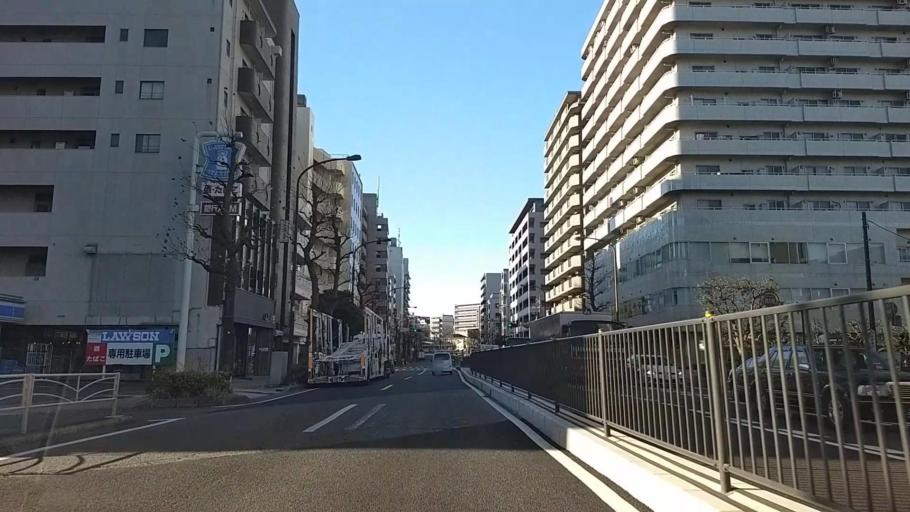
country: JP
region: Kanagawa
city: Yokohama
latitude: 35.4771
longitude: 139.6286
